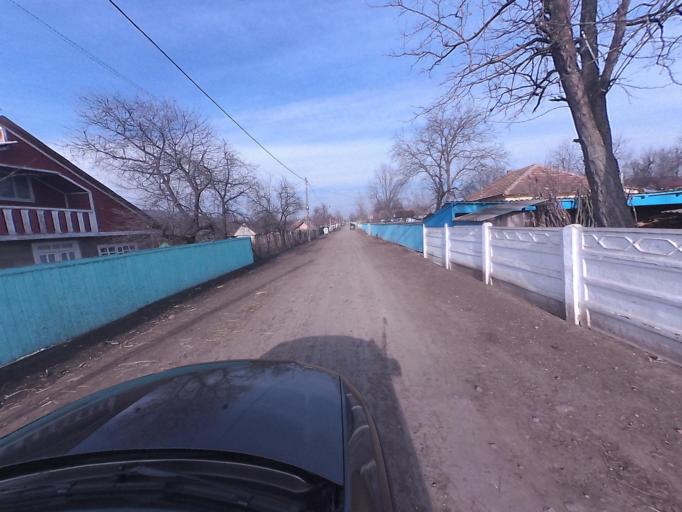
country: RO
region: Vaslui
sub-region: Comuna Solesti
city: Solesti
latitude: 46.8056
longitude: 27.7852
